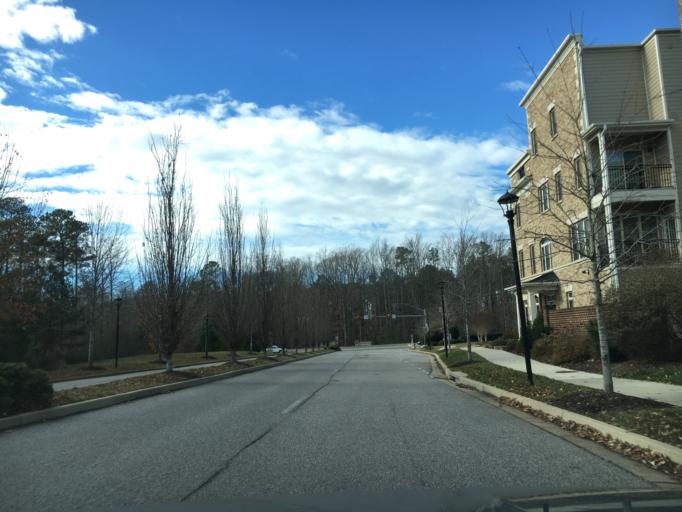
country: US
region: Virginia
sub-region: Henrico County
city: Short Pump
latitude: 37.6474
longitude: -77.6075
